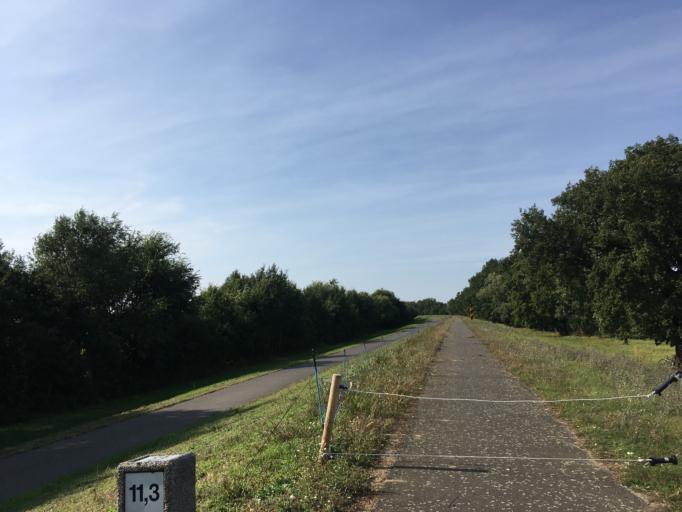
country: DE
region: Brandenburg
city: Vogelsang
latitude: 52.2481
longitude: 14.6931
